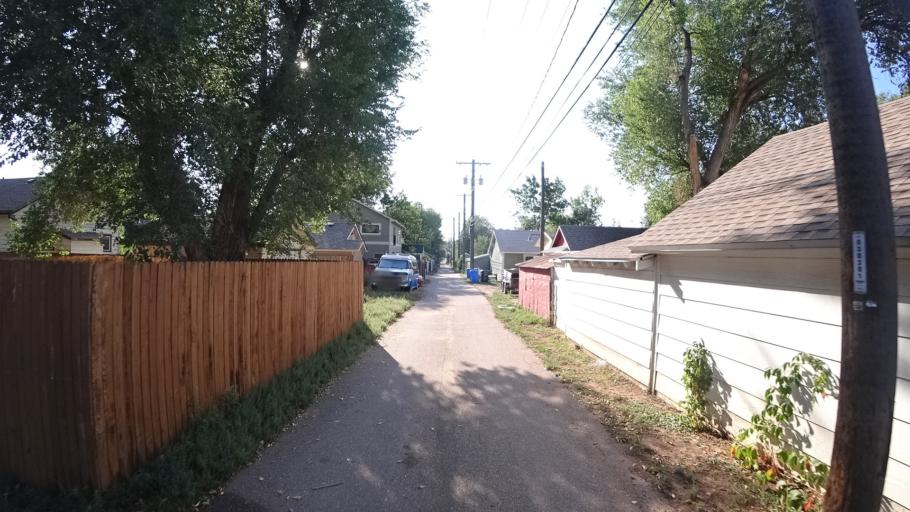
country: US
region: Colorado
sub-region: El Paso County
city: Manitou Springs
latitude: 38.8523
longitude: -104.8683
